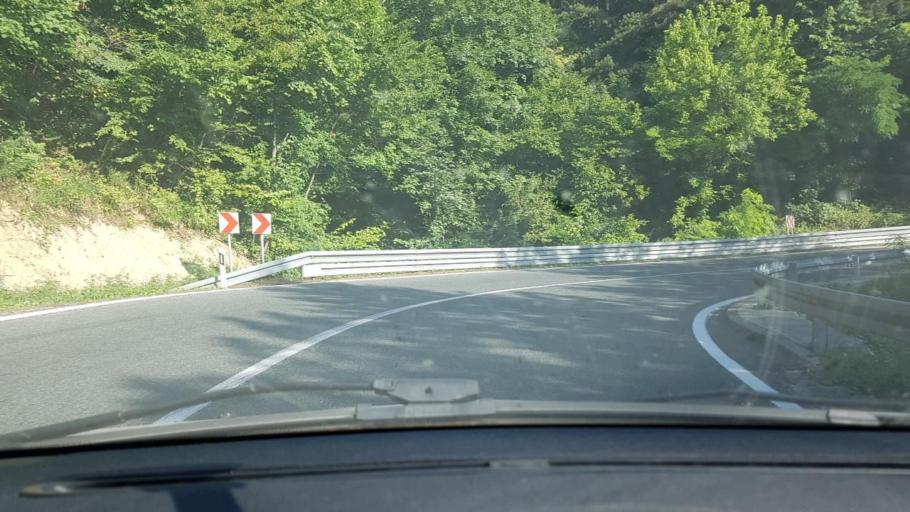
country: BA
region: Federation of Bosnia and Herzegovina
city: Ostrozac
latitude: 44.9017
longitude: 15.9362
